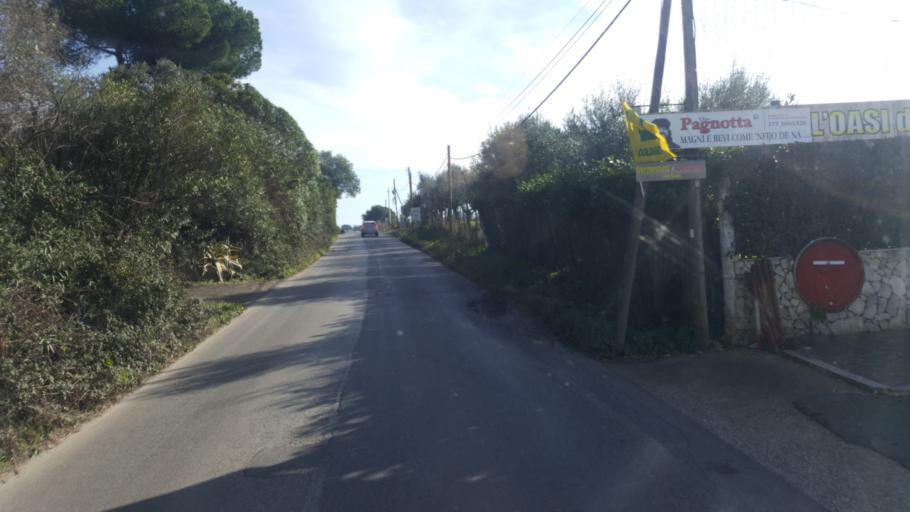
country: IT
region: Latium
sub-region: Citta metropolitana di Roma Capitale
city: Mantiglia di Ardea
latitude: 41.6816
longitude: 12.6185
